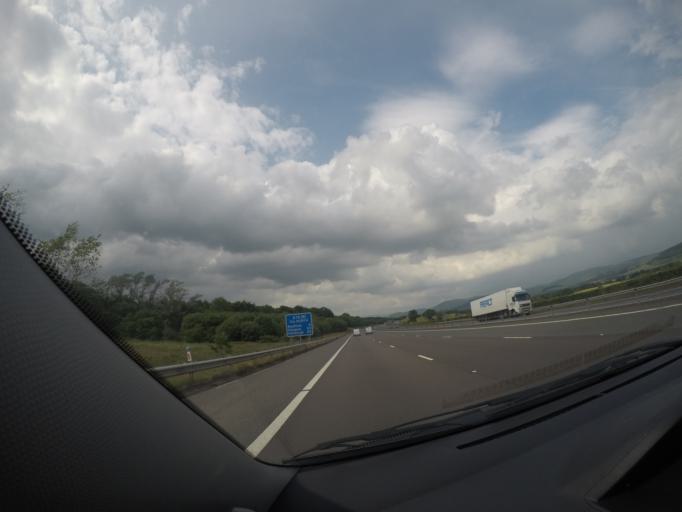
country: GB
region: Scotland
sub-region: Dumfries and Galloway
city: Lochmaben
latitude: 55.2266
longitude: -3.4133
